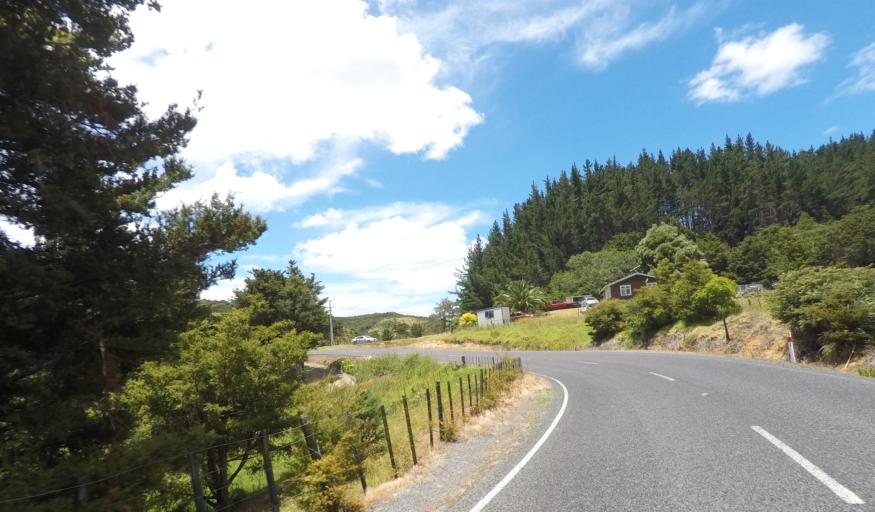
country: NZ
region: Northland
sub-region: Whangarei
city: Ngunguru
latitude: -35.5058
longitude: 174.4087
